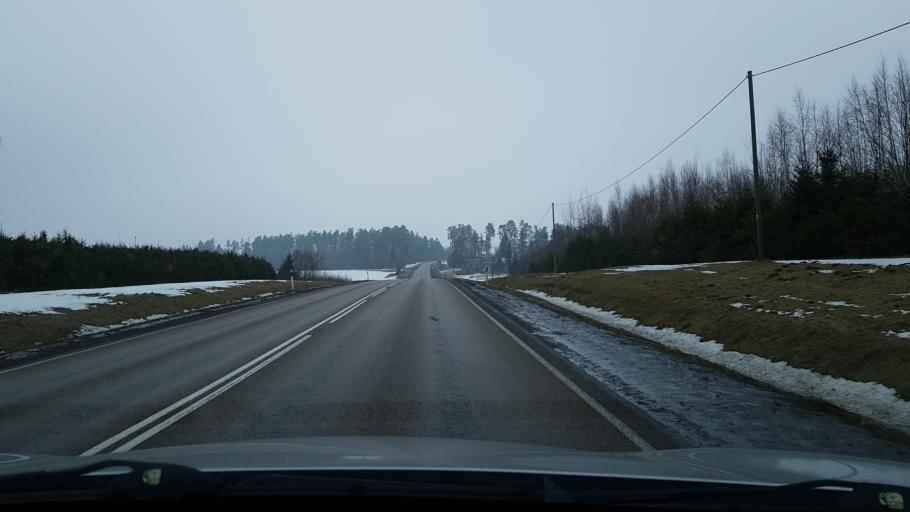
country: EE
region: Tartu
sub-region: Elva linn
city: Elva
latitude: 58.0779
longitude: 26.2071
